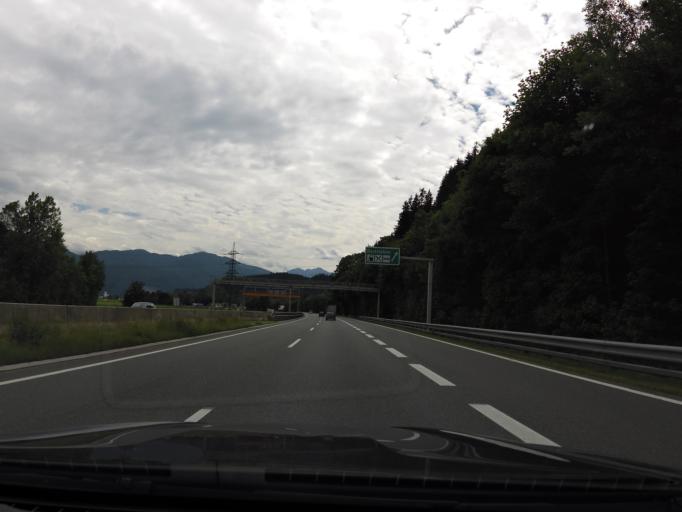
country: AT
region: Tyrol
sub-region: Politischer Bezirk Kufstein
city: Mariastein
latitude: 47.5233
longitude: 12.0709
